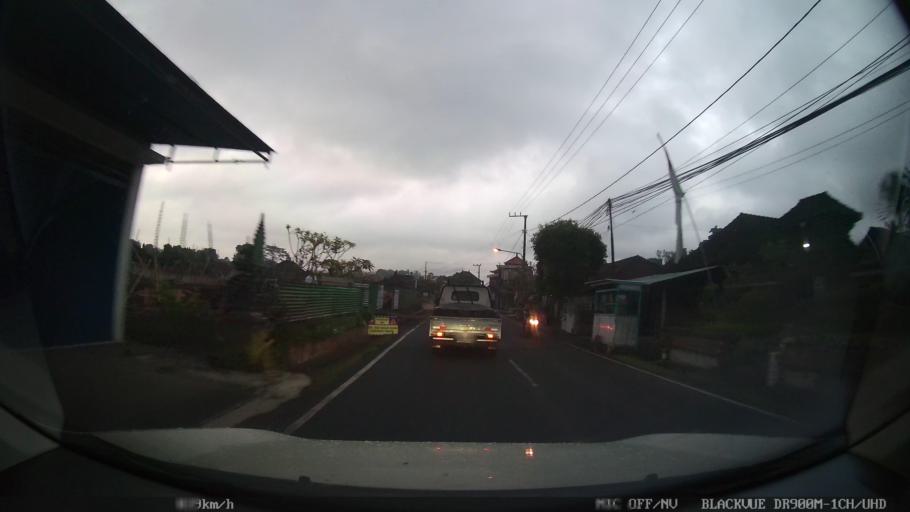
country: ID
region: Bali
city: Banjar Mambalkajanan
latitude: -8.5482
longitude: 115.2421
